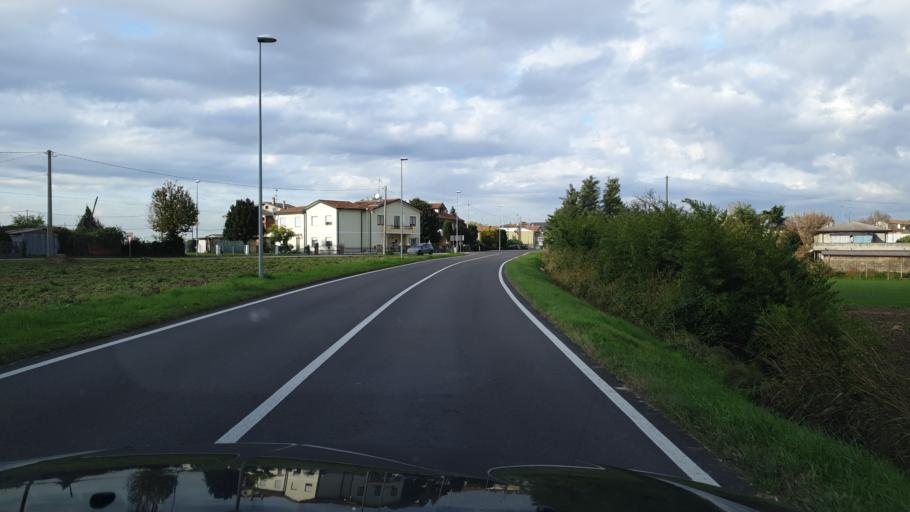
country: IT
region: Veneto
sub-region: Provincia di Rovigo
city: Villanova del Ghebbo Canton
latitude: 45.0488
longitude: 11.6458
